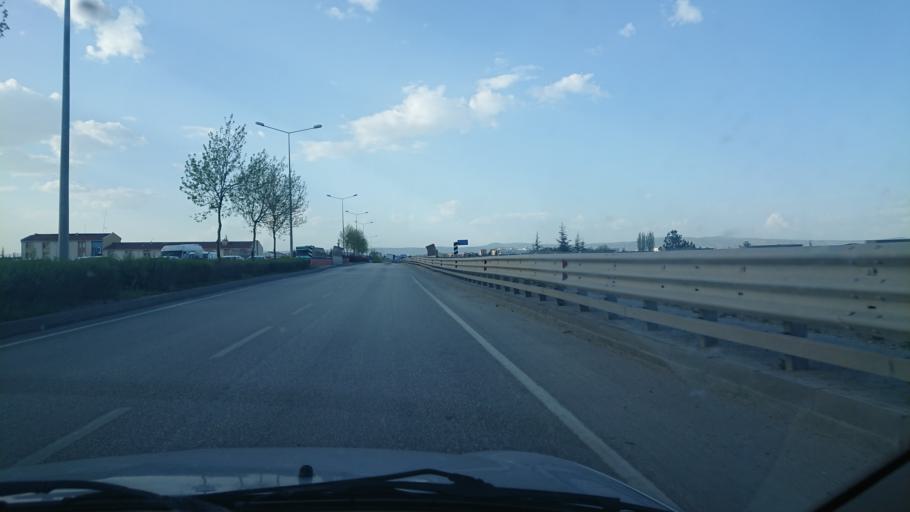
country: TR
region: Eskisehir
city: Eskisehir
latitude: 39.7740
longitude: 30.4839
